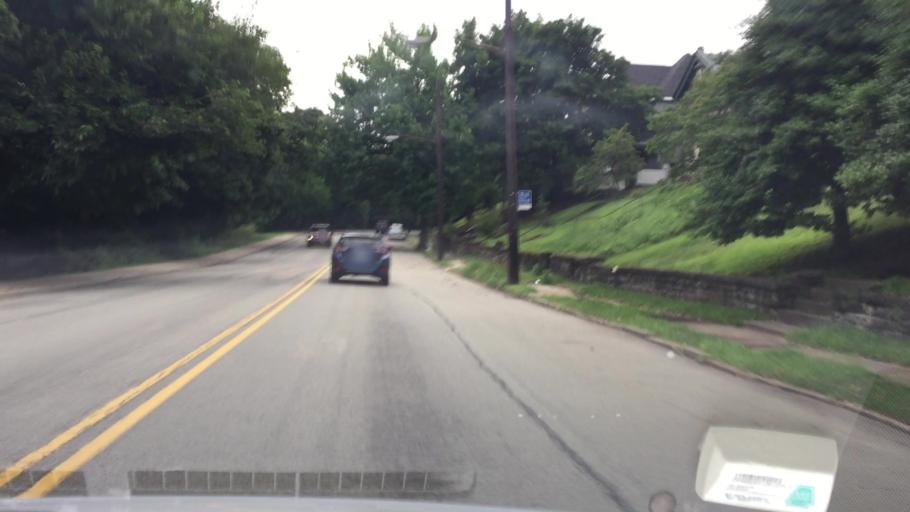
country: US
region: Pennsylvania
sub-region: Allegheny County
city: Millvale
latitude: 40.4809
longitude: -80.0133
